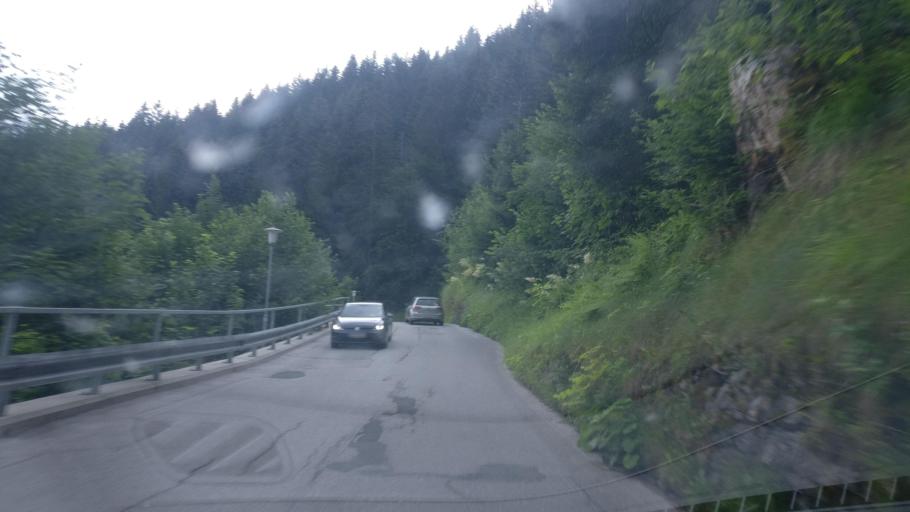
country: AT
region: Salzburg
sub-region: Politischer Bezirk Sankt Johann im Pongau
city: Bad Gastein
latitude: 47.1133
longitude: 13.1379
